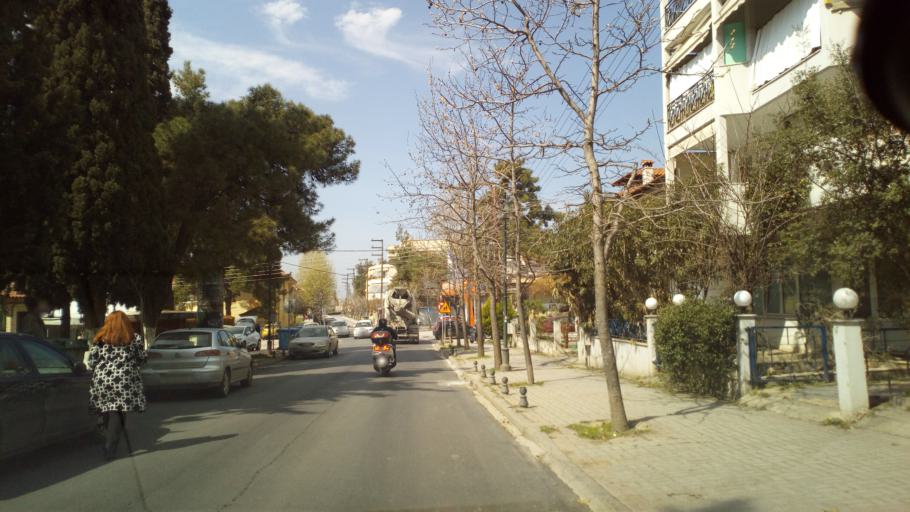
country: GR
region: Central Macedonia
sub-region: Nomos Thessalonikis
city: Thermi
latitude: 40.5493
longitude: 23.0231
